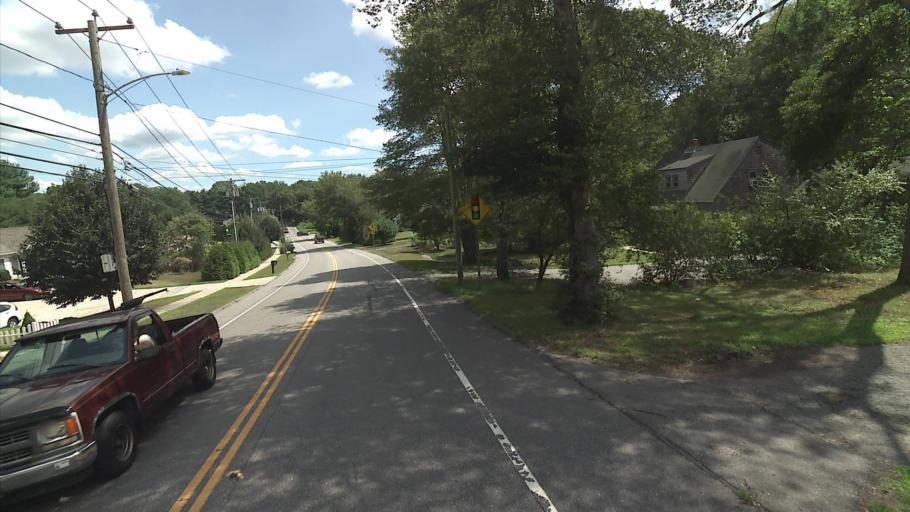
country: US
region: Connecticut
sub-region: New London County
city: Poquonock Bridge
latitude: 41.3517
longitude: -72.0004
